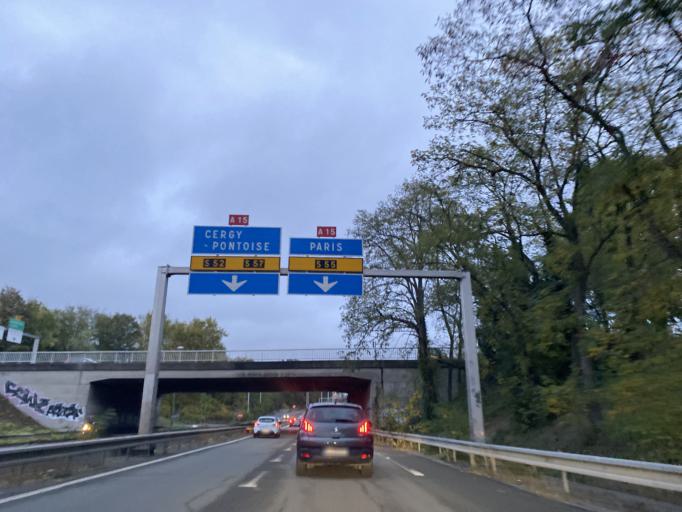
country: FR
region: Ile-de-France
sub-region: Departement du Val-d'Oise
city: Saint-Gratien
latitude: 48.9552
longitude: 2.2761
